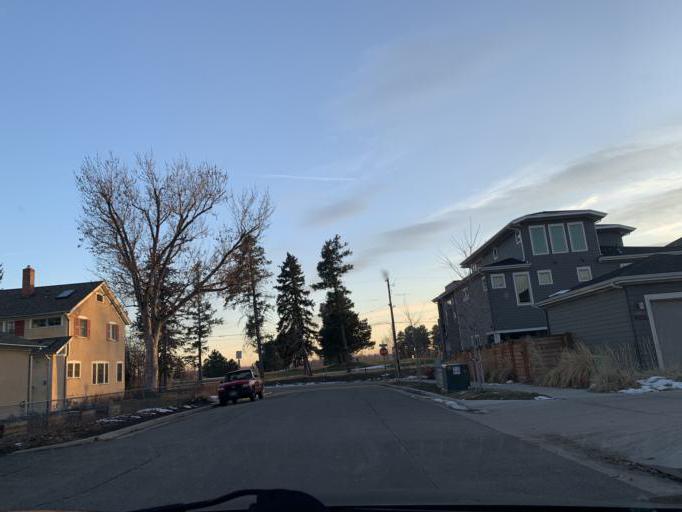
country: US
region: Colorado
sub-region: Adams County
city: Berkley
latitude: 39.7880
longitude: -105.0451
